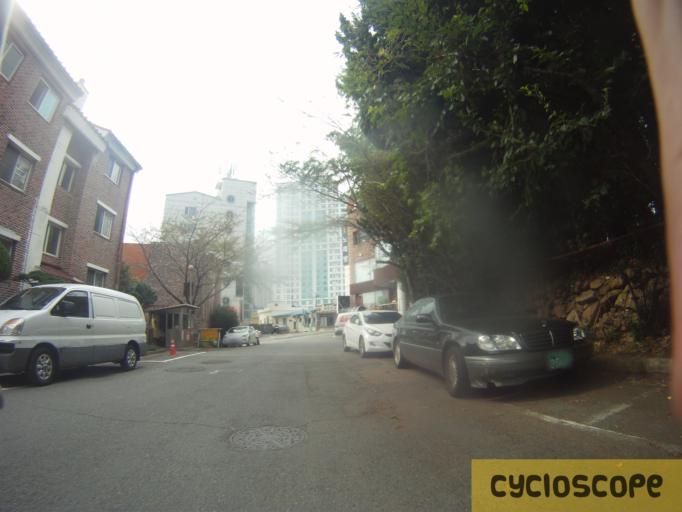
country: KR
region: Busan
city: Kijang
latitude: 35.1593
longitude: 129.1696
